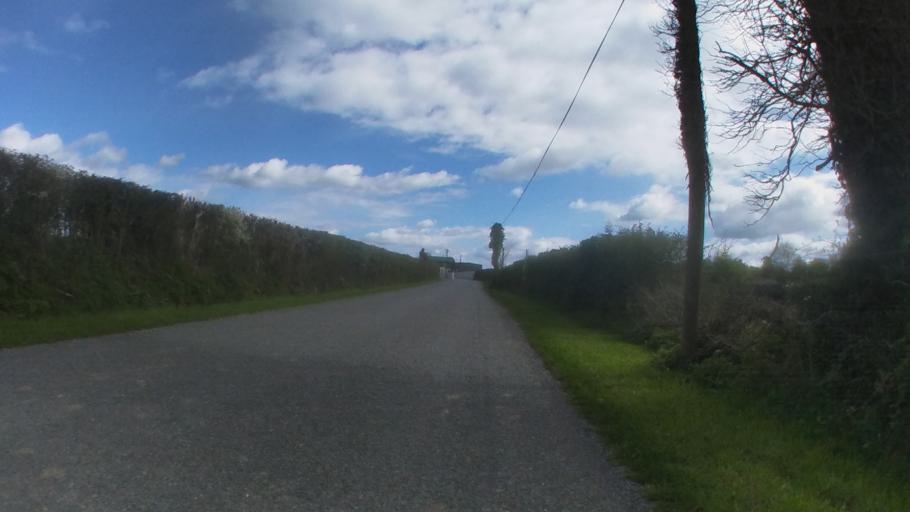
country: IE
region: Leinster
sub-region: Kilkenny
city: Kilkenny
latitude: 52.7153
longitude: -7.2285
